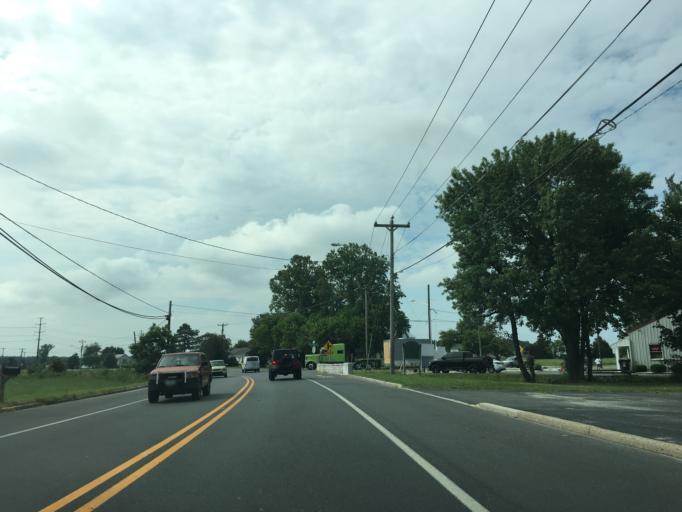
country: US
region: Delaware
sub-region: Sussex County
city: Millsboro
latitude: 38.5533
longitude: -75.2488
